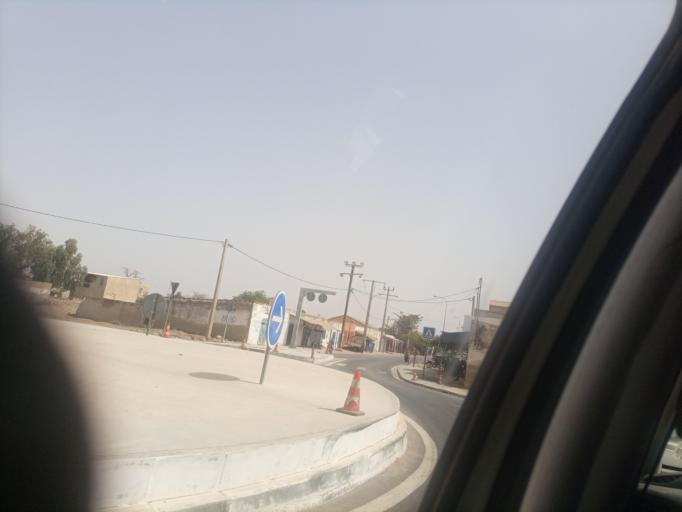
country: SN
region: Fatick
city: Foundiougne
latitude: 14.1299
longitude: -16.4668
